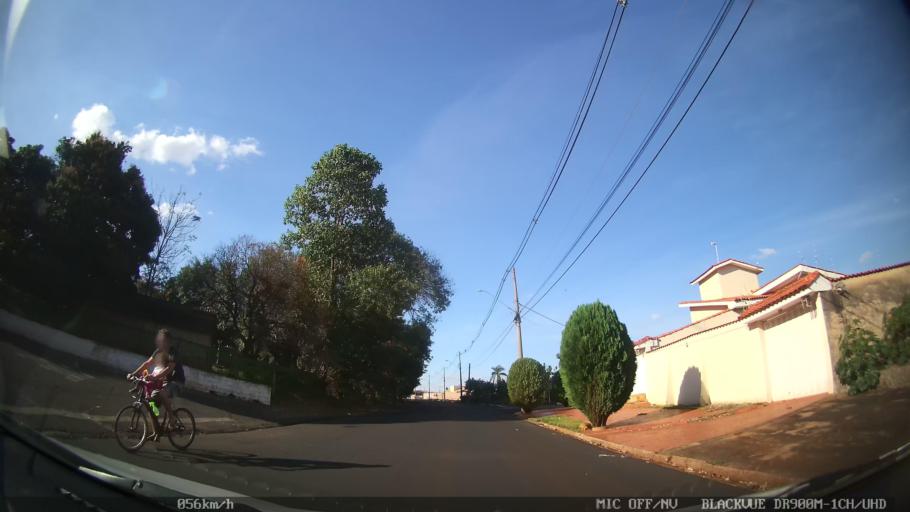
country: BR
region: Sao Paulo
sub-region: Ribeirao Preto
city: Ribeirao Preto
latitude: -21.2077
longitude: -47.7787
